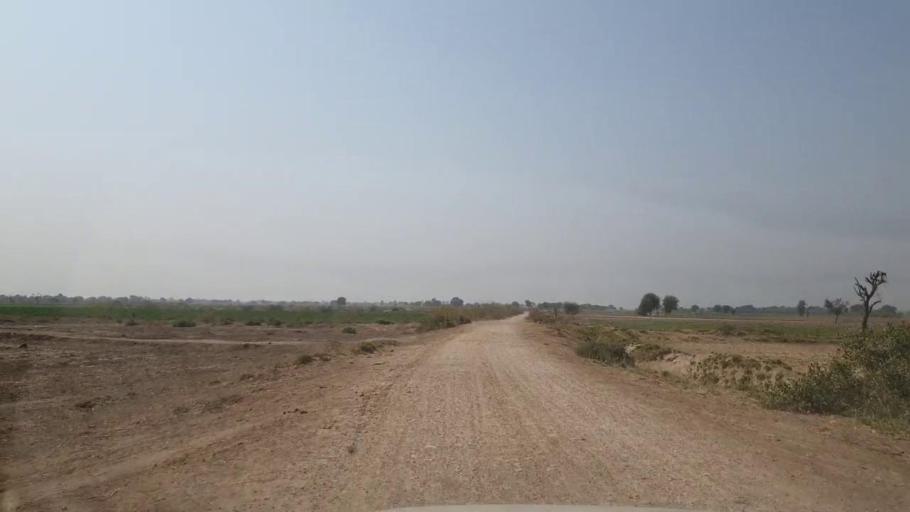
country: PK
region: Sindh
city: Mirpur Khas
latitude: 25.6547
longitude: 69.1261
